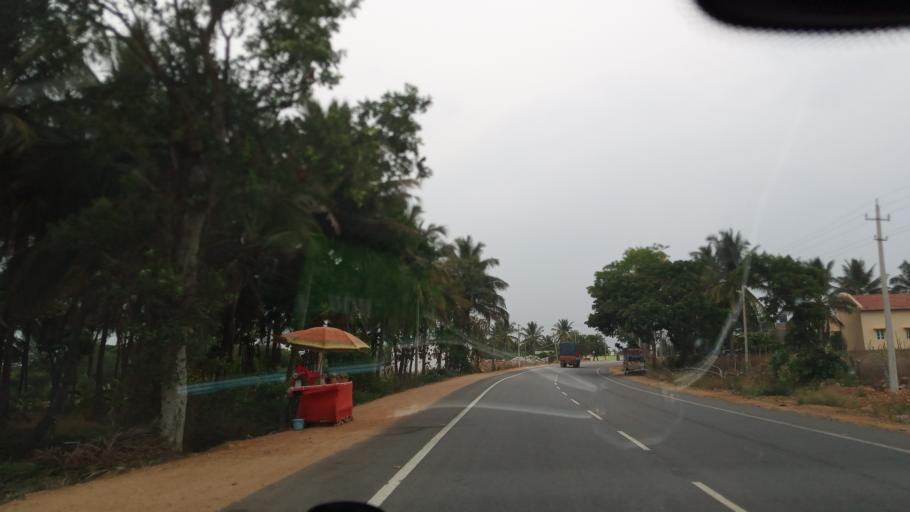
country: IN
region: Karnataka
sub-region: Mandya
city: Nagamangala
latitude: 12.8048
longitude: 76.7525
